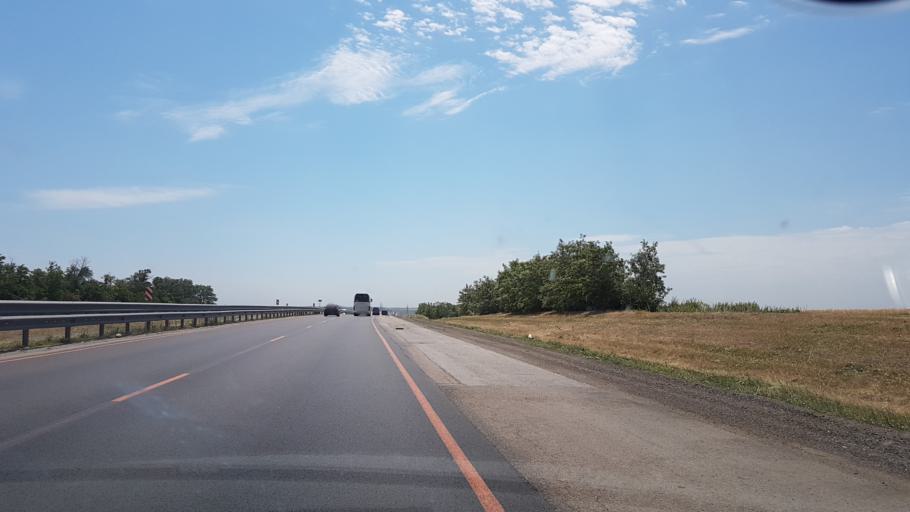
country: RU
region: Rostov
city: Ayutinskiy
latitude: 47.8043
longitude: 40.1702
